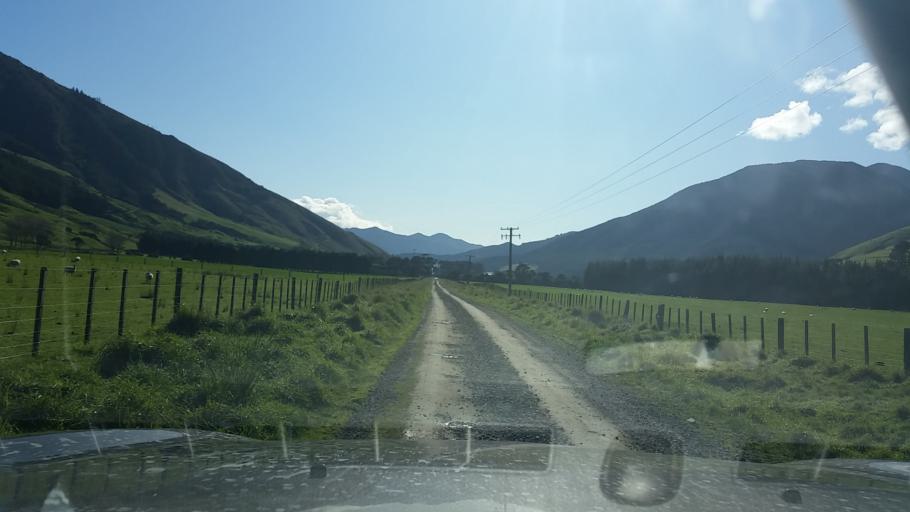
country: NZ
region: Marlborough
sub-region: Marlborough District
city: Picton
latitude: -41.1273
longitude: 174.0402
